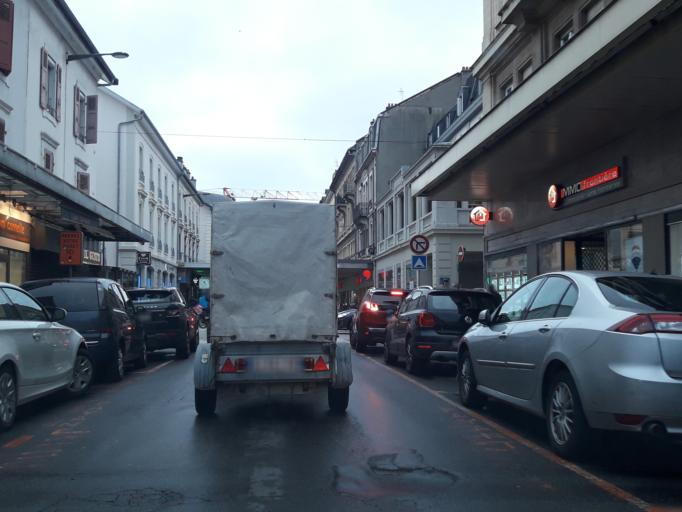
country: FR
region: Rhone-Alpes
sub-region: Departement de la Haute-Savoie
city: Annemasse
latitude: 46.1936
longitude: 6.2336
